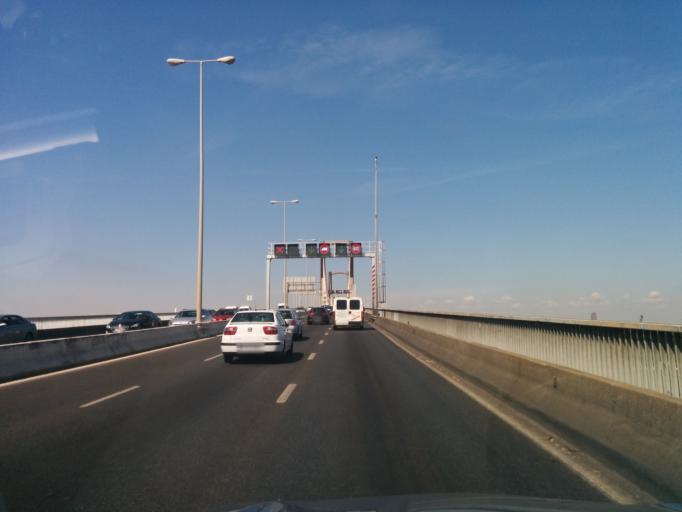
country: ES
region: Andalusia
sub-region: Provincia de Sevilla
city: Gelves
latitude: 37.3447
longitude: -5.9879
